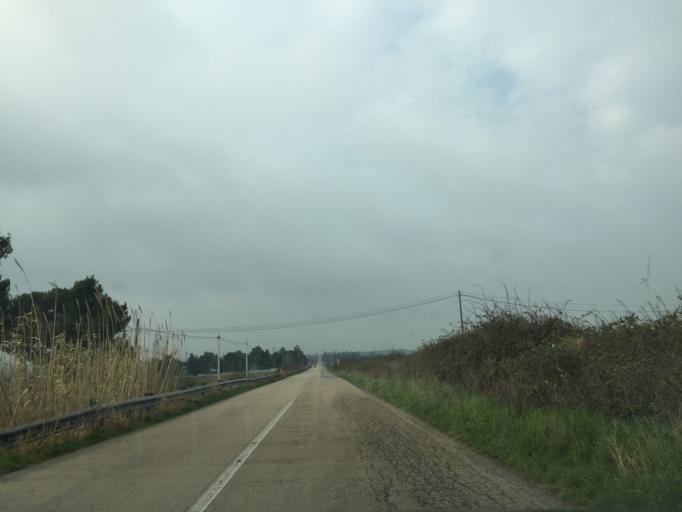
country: IT
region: Apulia
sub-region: Provincia di Foggia
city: Troia
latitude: 41.3884
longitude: 15.3966
